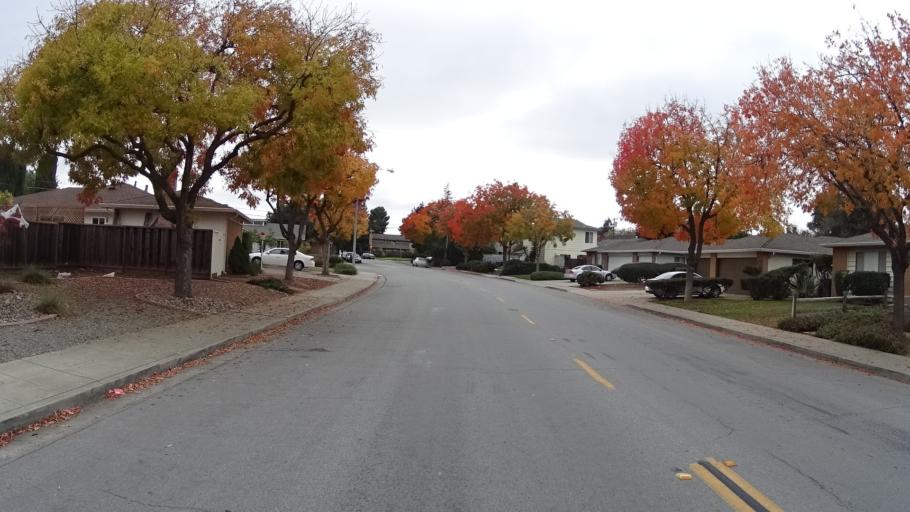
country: US
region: California
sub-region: Santa Clara County
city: Sunnyvale
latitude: 37.3544
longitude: -122.0281
